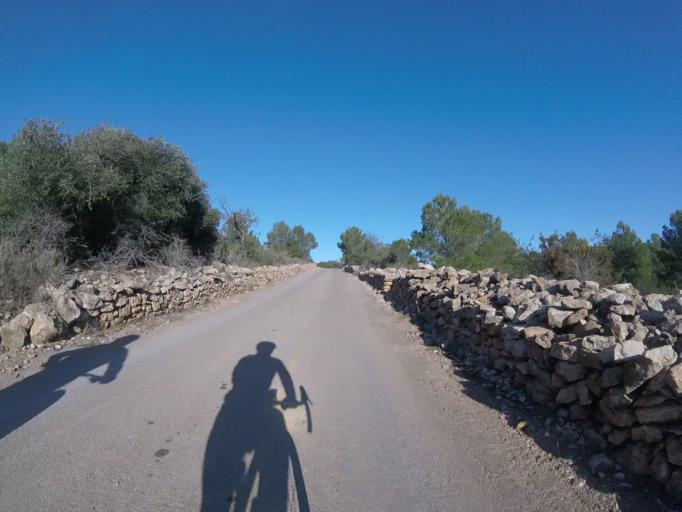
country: ES
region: Valencia
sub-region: Provincia de Castello
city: Alcala de Xivert
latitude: 40.2698
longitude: 0.2072
